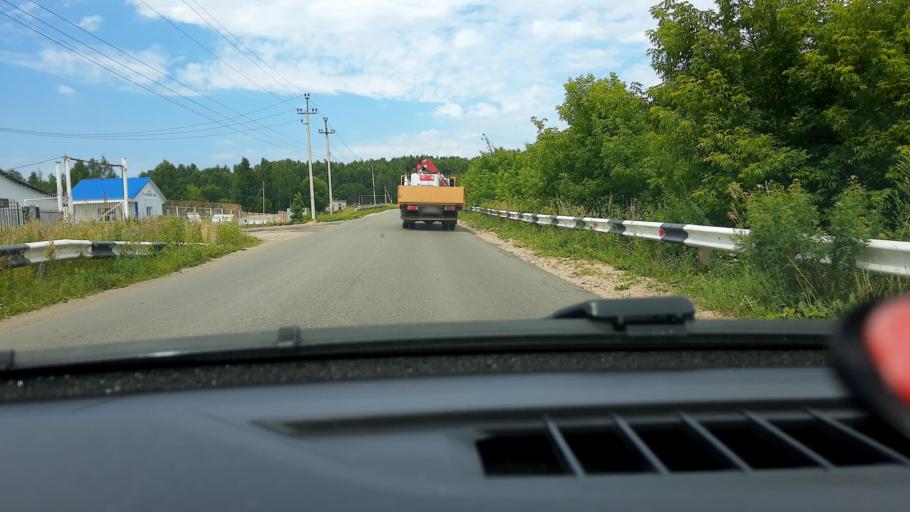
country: RU
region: Nizjnij Novgorod
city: Bogorodsk
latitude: 56.1383
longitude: 43.5890
